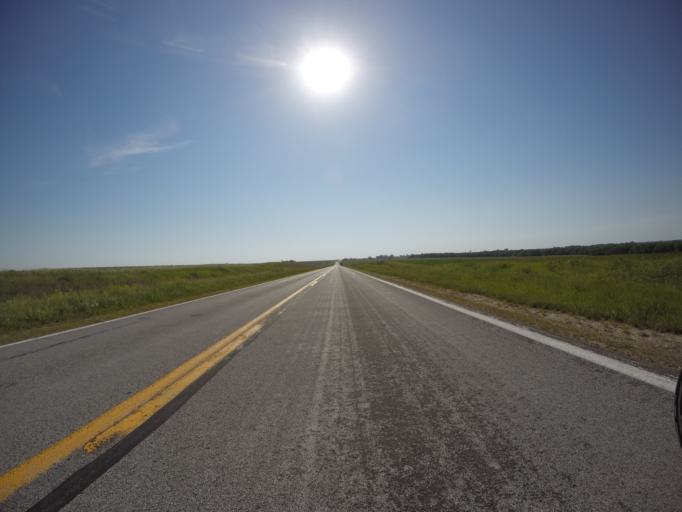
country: US
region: Nebraska
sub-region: Pawnee County
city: Pawnee City
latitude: 40.0447
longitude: -96.3816
